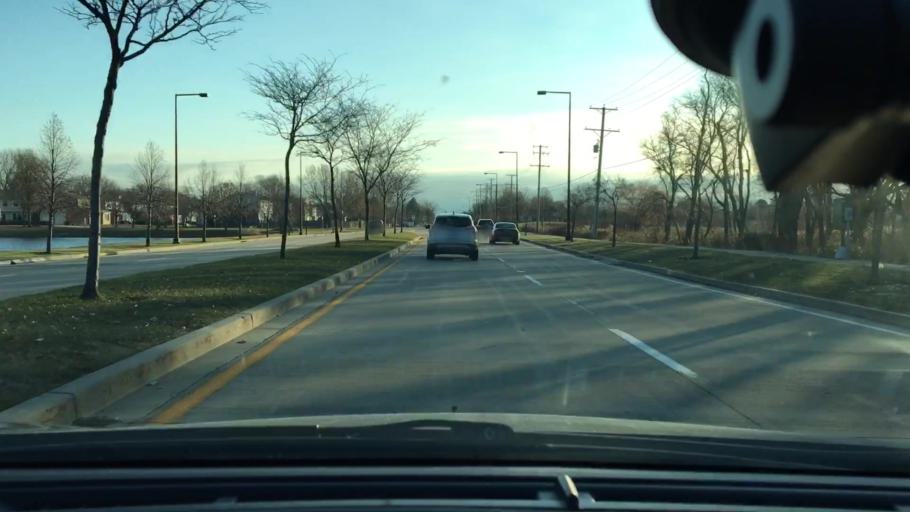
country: US
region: Illinois
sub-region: Cook County
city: Buffalo Grove
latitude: 42.1717
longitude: -87.9700
